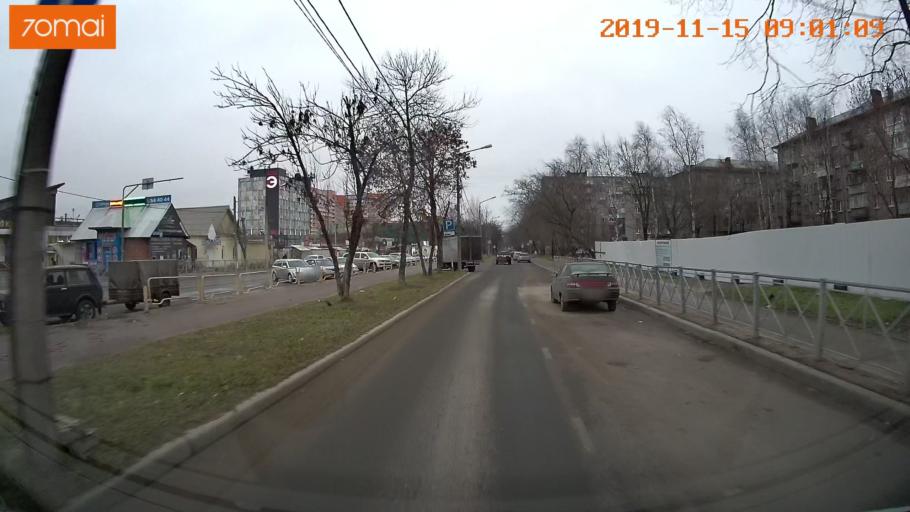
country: RU
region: Vologda
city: Cherepovets
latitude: 59.1307
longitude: 37.9252
